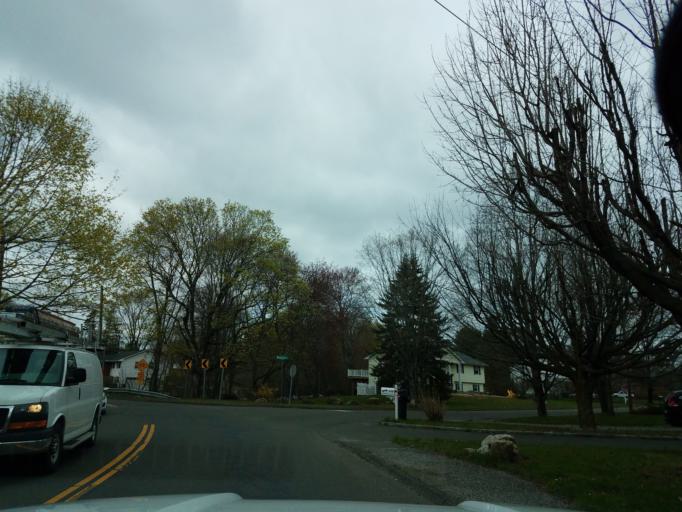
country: US
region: Connecticut
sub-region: Fairfield County
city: Darien
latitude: 41.0853
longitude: -73.4427
